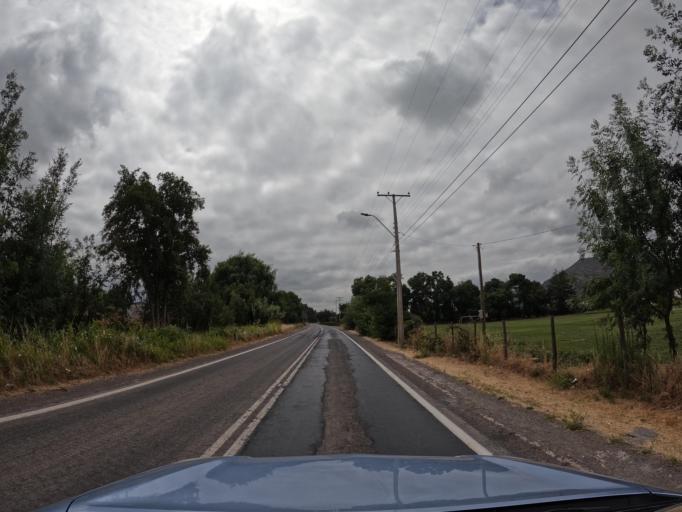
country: CL
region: Maule
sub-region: Provincia de Curico
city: Teno
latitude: -34.7502
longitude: -71.2301
